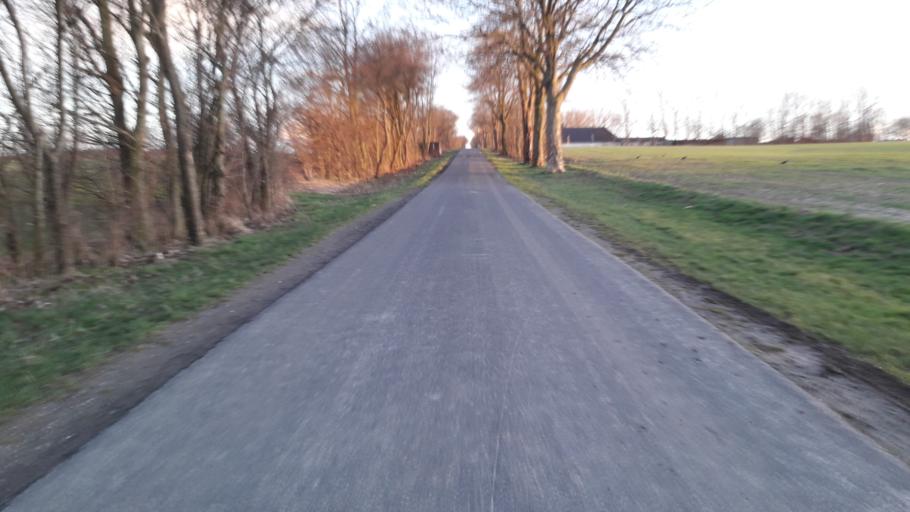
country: DE
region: North Rhine-Westphalia
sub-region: Regierungsbezirk Detmold
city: Paderborn
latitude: 51.6961
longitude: 8.7714
